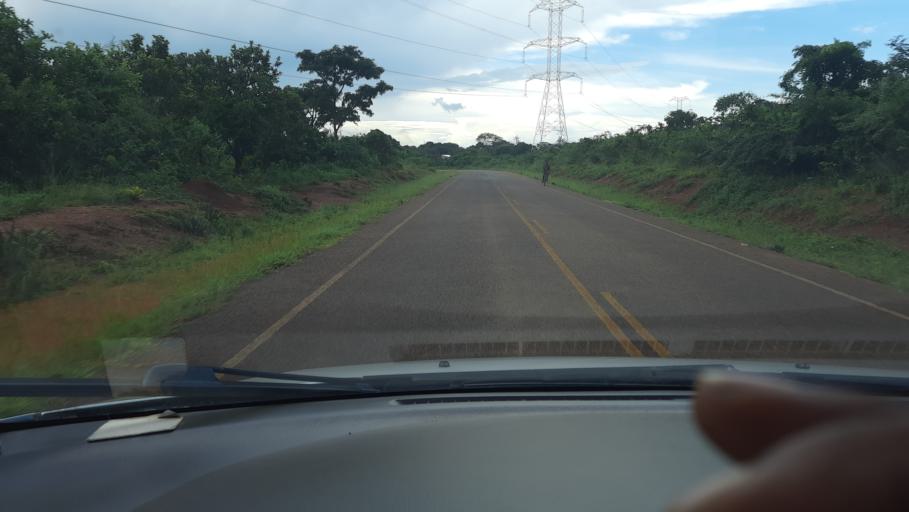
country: UG
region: Central Region
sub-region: Nakasongola District
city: Nakasongola
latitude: 1.3244
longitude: 32.4286
